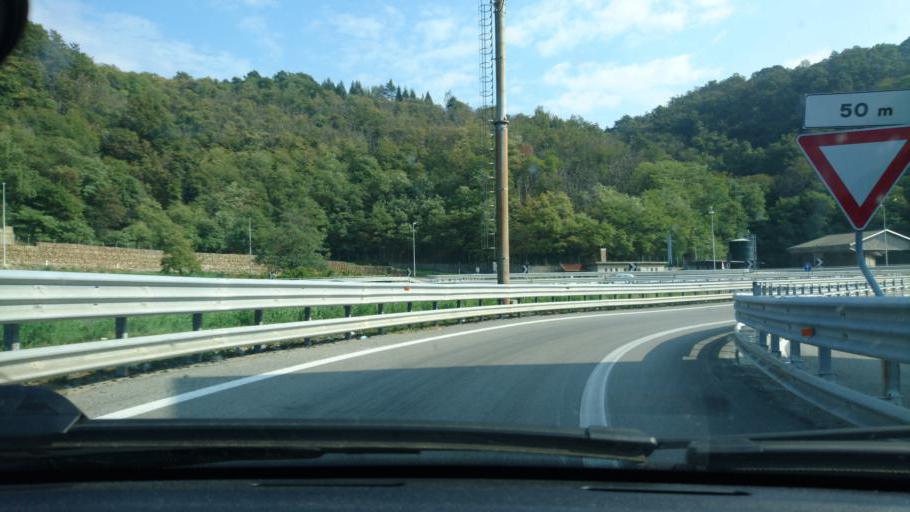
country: IT
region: Liguria
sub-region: Provincia di Savona
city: Altare
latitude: 44.3452
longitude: 8.3230
